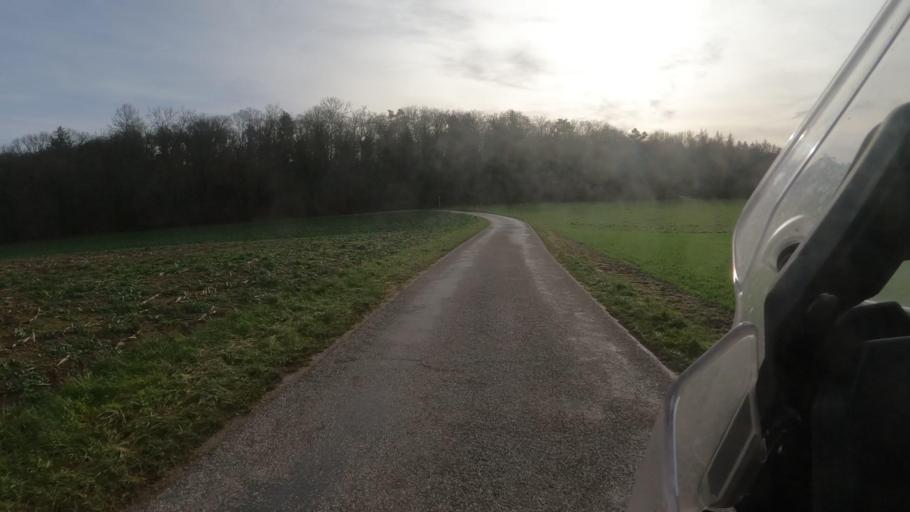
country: CH
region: Zurich
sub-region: Bezirk Buelach
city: Glattfelden
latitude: 47.5445
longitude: 8.5096
